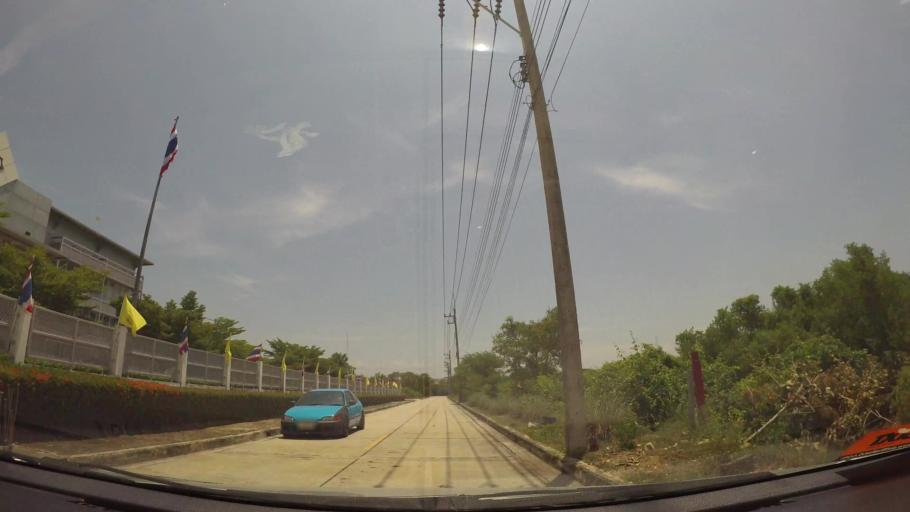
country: TH
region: Chon Buri
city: Chon Buri
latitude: 13.3395
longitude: 100.9452
